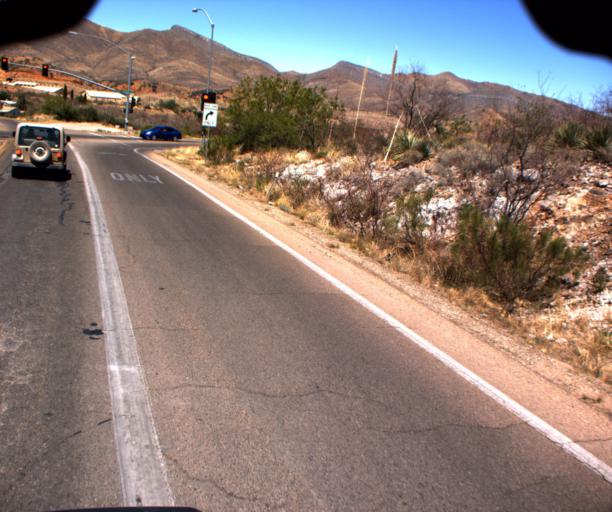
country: US
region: Arizona
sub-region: Cochise County
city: Bisbee
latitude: 31.4197
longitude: -109.8960
